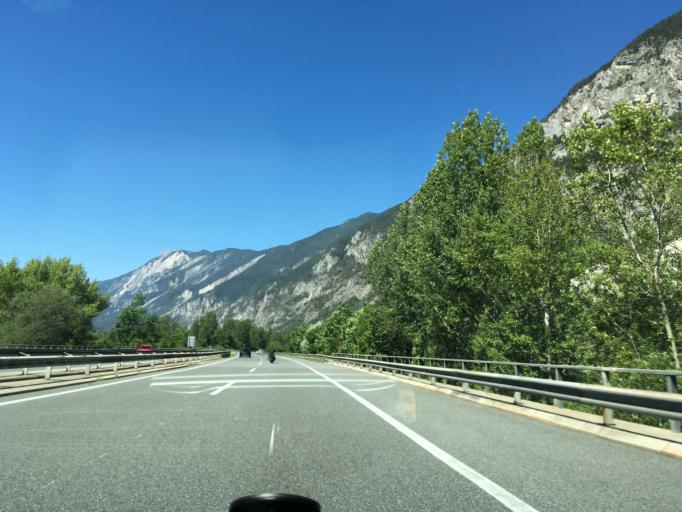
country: AT
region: Tyrol
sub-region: Politischer Bezirk Imst
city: Silz
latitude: 47.2735
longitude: 10.9385
